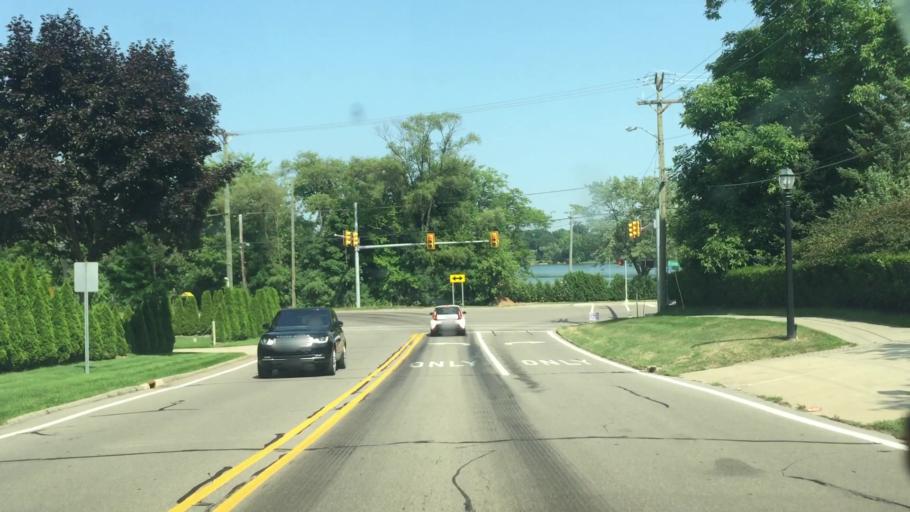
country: US
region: Michigan
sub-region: Oakland County
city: Franklin
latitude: 42.5525
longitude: -83.3035
